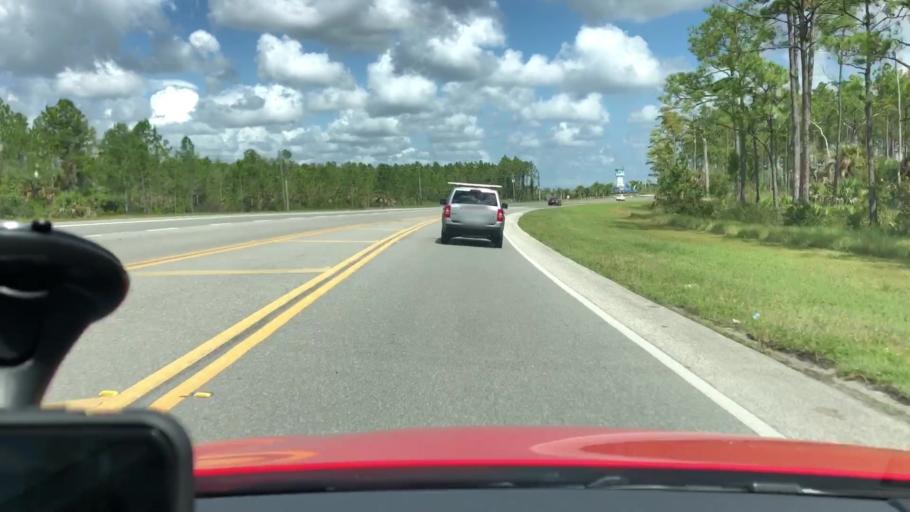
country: US
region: Florida
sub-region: Volusia County
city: Holly Hill
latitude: 29.2096
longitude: -81.1198
